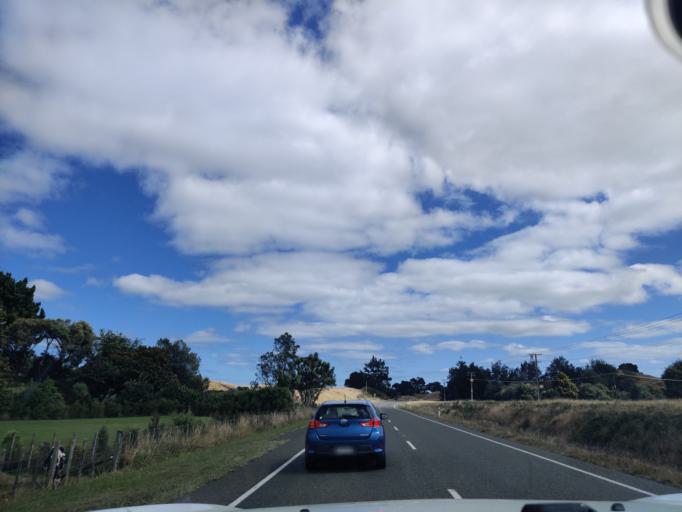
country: NZ
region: Manawatu-Wanganui
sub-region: Horowhenua District
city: Foxton
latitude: -40.4124
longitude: 175.3903
